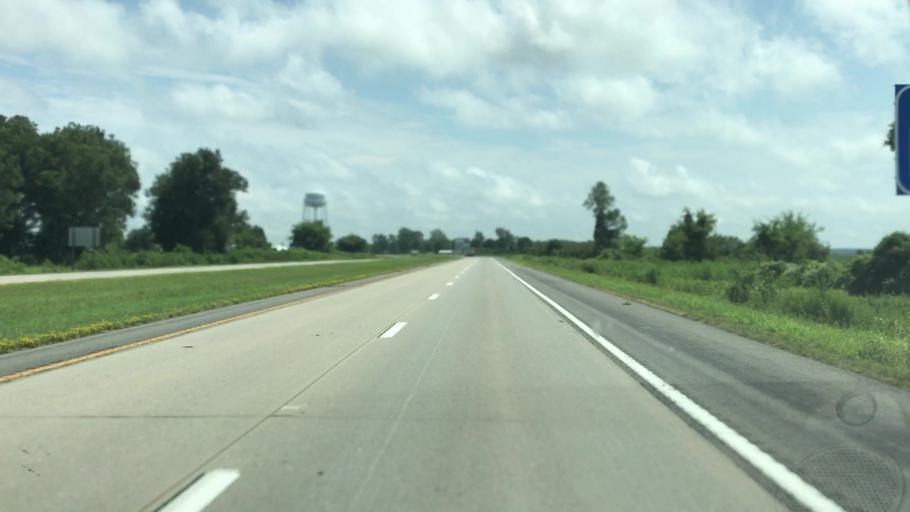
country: US
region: Missouri
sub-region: Pemiscot County
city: Caruthersville
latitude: 36.1596
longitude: -89.6769
